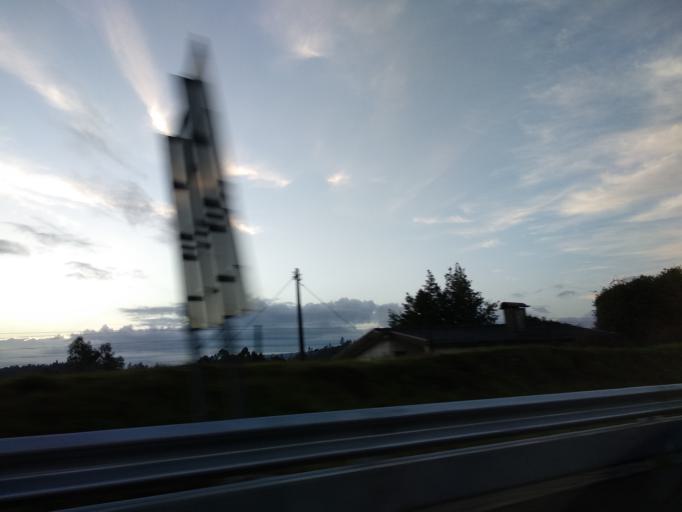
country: PT
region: Braga
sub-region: Braga
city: Oliveira
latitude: 41.4875
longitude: -8.4667
